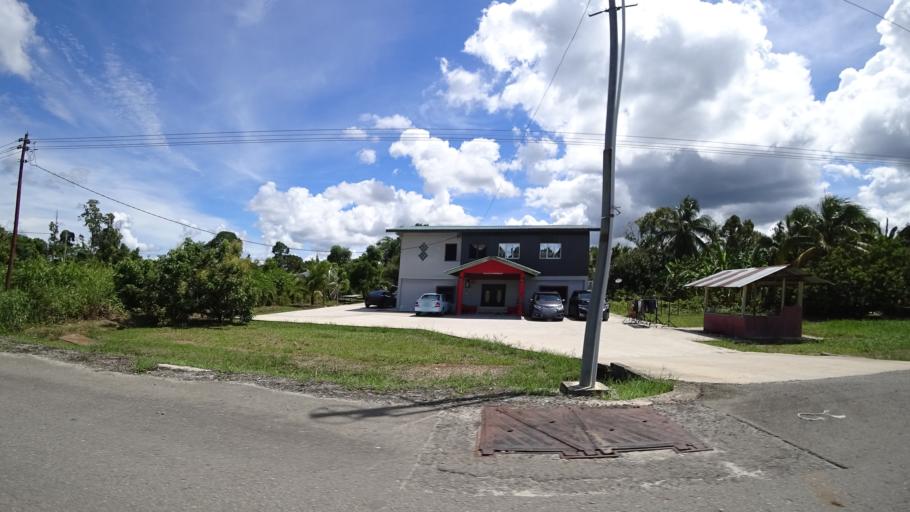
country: MY
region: Sarawak
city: Limbang
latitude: 4.8251
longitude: 114.9169
